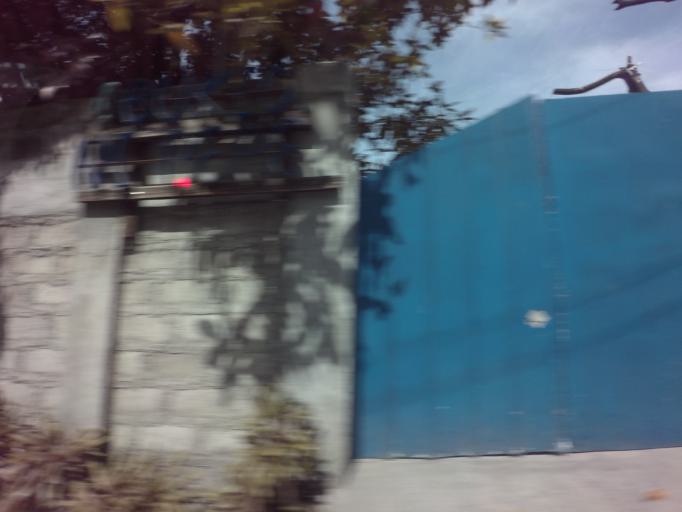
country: PH
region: Calabarzon
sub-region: Province of Rizal
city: Pateros
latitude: 14.5328
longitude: 121.0767
